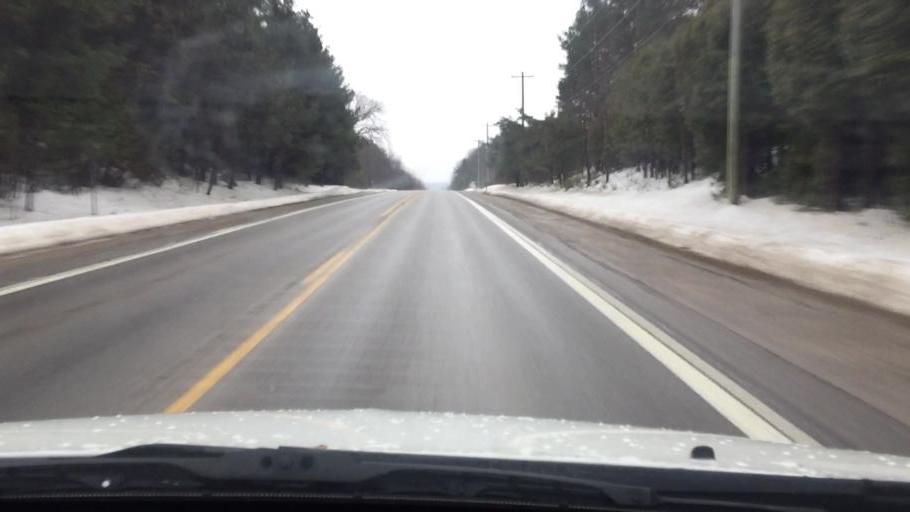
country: US
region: Michigan
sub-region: Charlevoix County
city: Charlevoix
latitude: 45.2665
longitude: -85.2032
